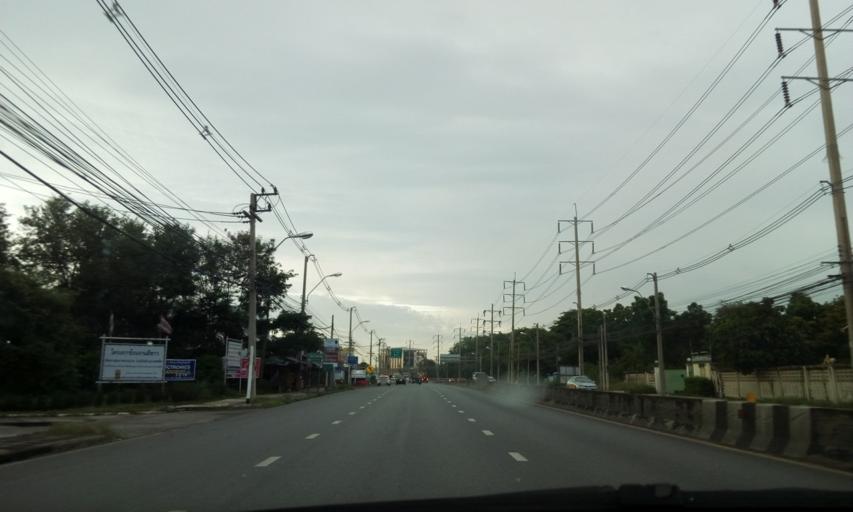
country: TH
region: Phra Nakhon Si Ayutthaya
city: Ban Bang Kadi Pathum Thani
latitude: 13.9545
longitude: 100.5493
